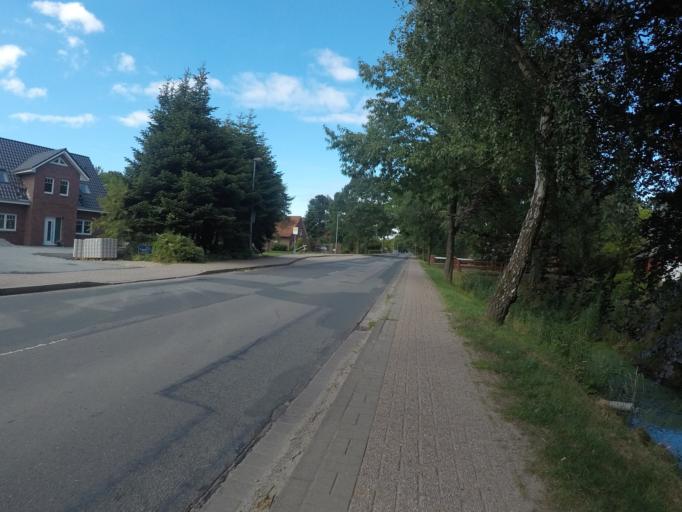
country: DE
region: Lower Saxony
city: Osterbruch
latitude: 53.7791
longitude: 8.9421
